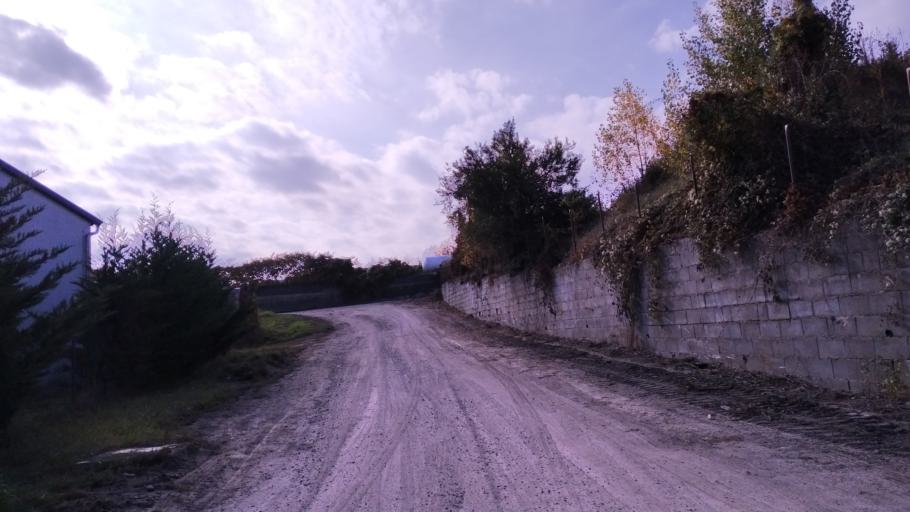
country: HU
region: Pest
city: Pomaz
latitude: 47.6430
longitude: 19.0409
